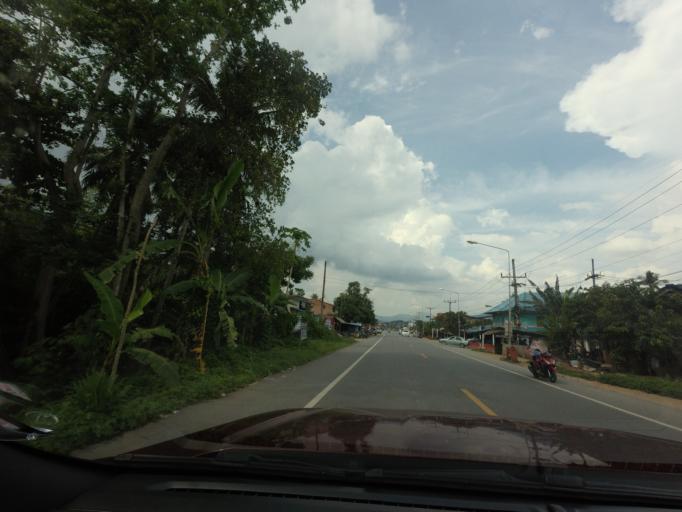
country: TH
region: Yala
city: Ban Nang Sata
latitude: 6.2592
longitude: 101.2534
